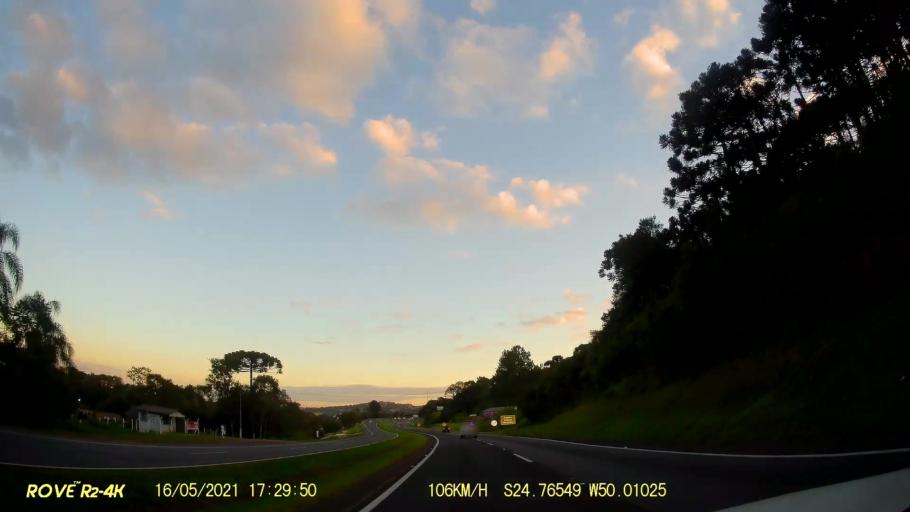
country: BR
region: Parana
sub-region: Castro
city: Castro
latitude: -24.7658
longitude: -50.0105
